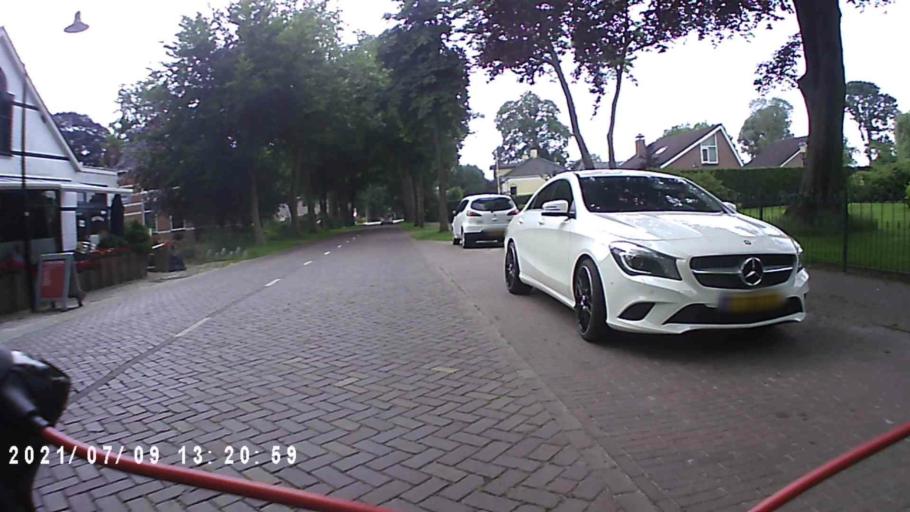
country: NL
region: Groningen
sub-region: Gemeente Vlagtwedde
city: Vlagtwedde
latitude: 53.1121
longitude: 7.1617
